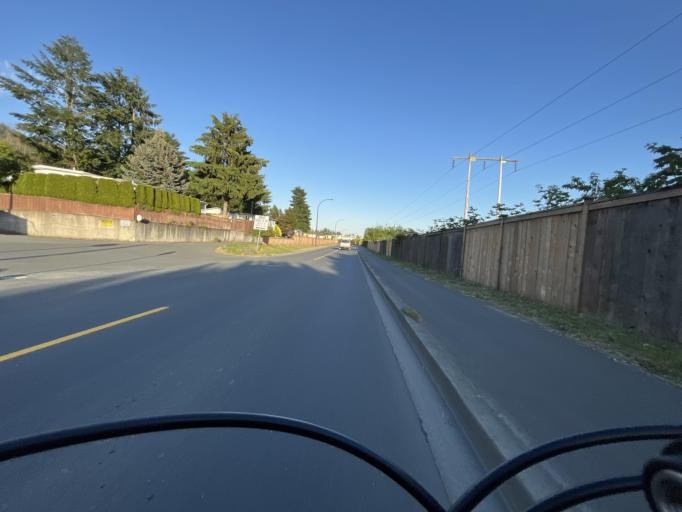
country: CA
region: British Columbia
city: Langford
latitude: 48.4594
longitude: -123.5470
